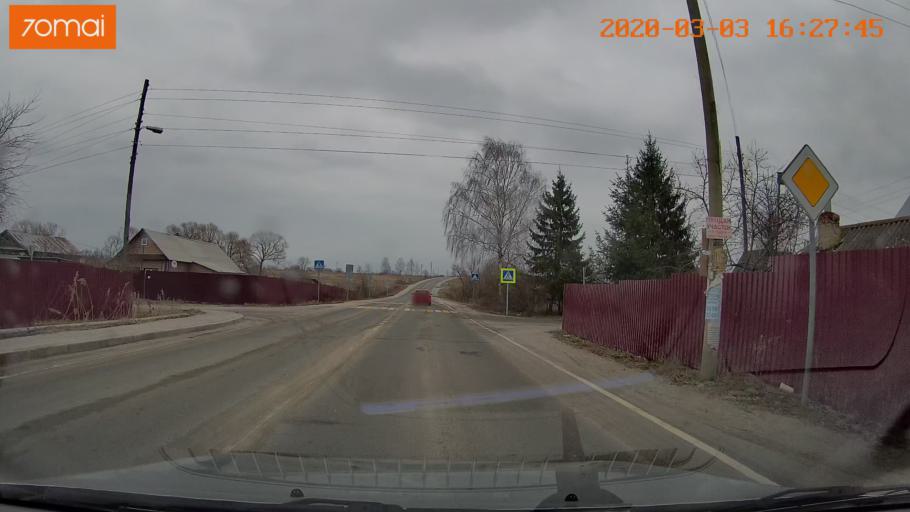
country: RU
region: Moskovskaya
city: Konobeyevo
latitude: 55.4368
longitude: 38.6755
